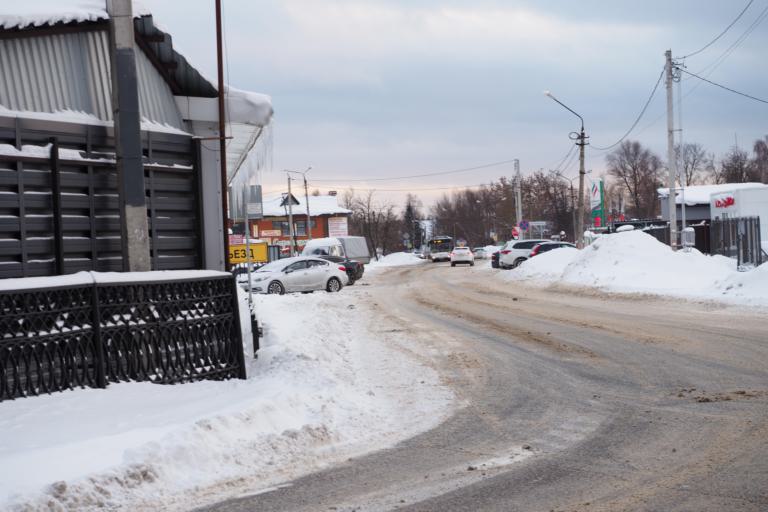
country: RU
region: Moskovskaya
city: Yegor'yevsk
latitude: 55.3761
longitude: 39.0349
